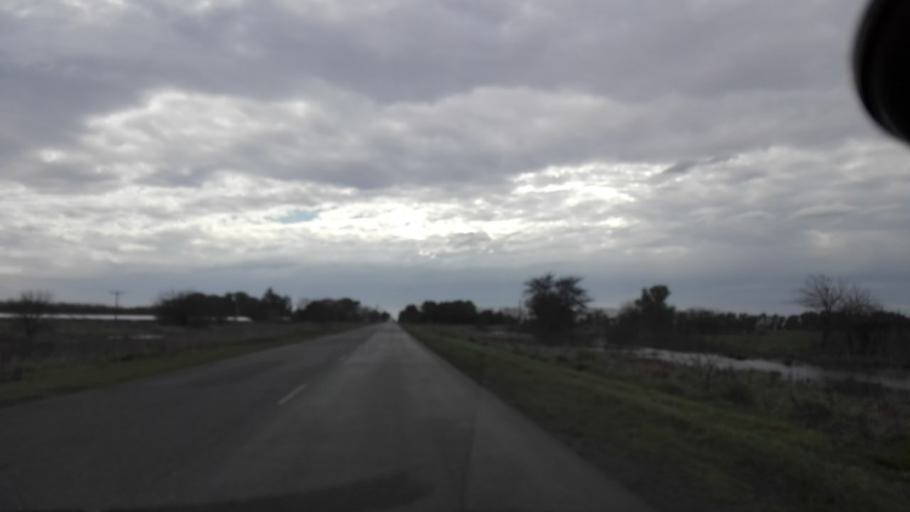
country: AR
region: Buenos Aires
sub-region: Partido de Las Flores
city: Las Flores
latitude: -36.2268
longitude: -59.0446
